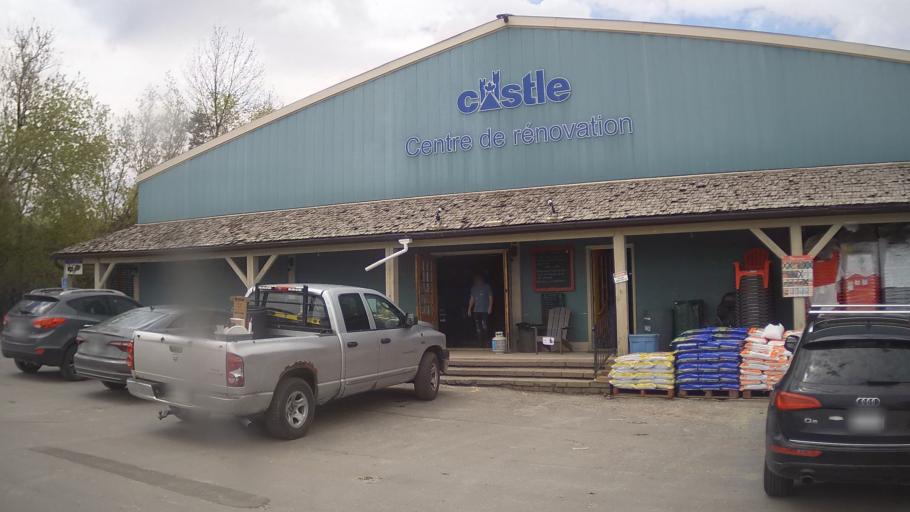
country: CA
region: Quebec
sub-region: Monteregie
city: Hudson
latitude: 45.4600
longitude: -74.1425
